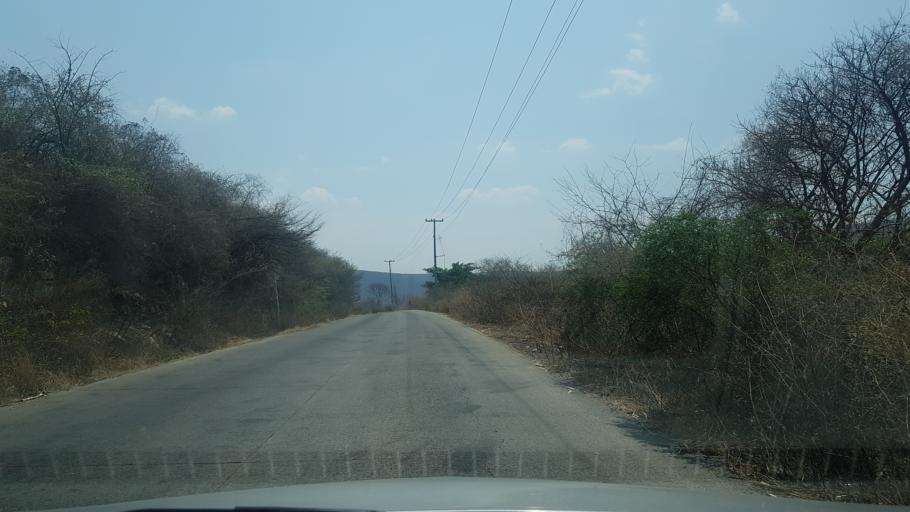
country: MX
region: Morelos
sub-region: Tlaltizapan de Zapata
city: Colonia Palo Prieto (Chipitongo)
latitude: 18.7438
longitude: -99.1129
